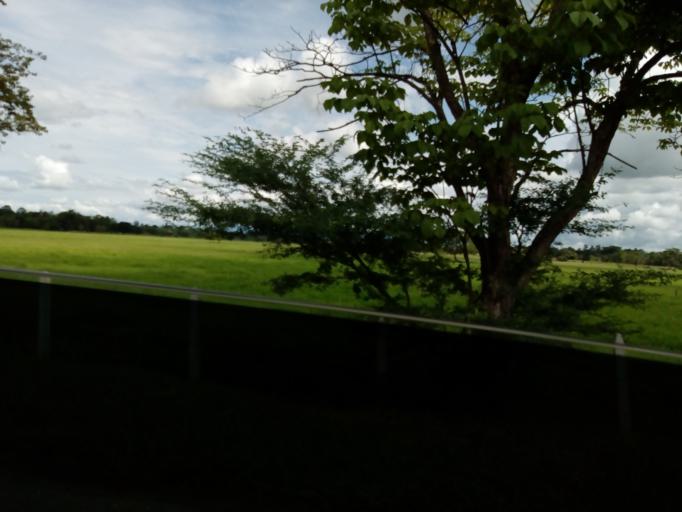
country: CO
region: Boyaca
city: Puerto Boyaca
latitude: 5.9424
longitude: -74.5699
